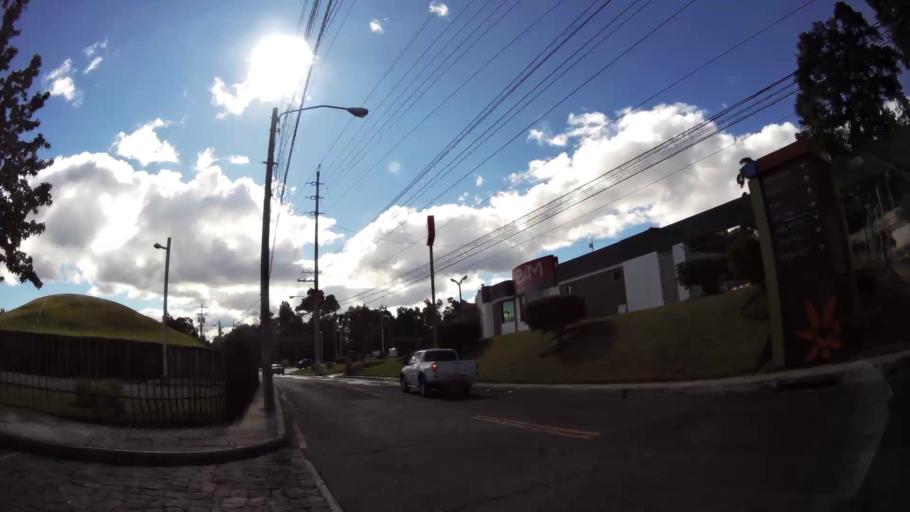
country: GT
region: Guatemala
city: Guatemala City
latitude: 14.6219
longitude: -90.5567
